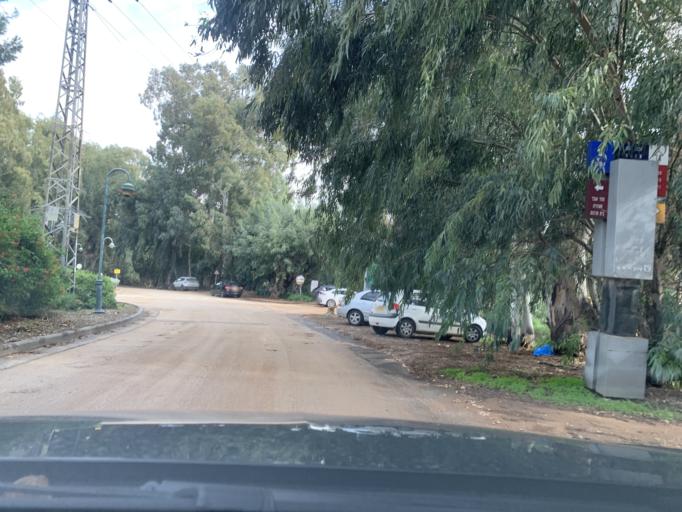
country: PS
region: West Bank
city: Qalqilyah
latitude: 32.1954
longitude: 34.9473
